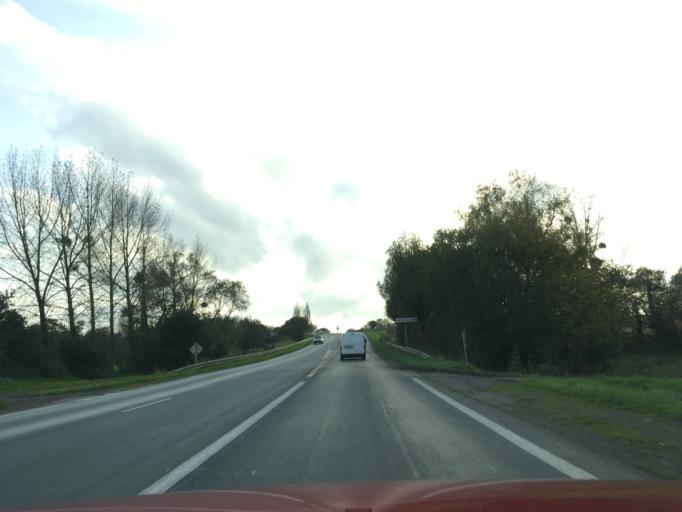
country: FR
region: Lower Normandy
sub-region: Departement de la Manche
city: Saint-Pair-sur-Mer
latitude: 48.8228
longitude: -1.5492
